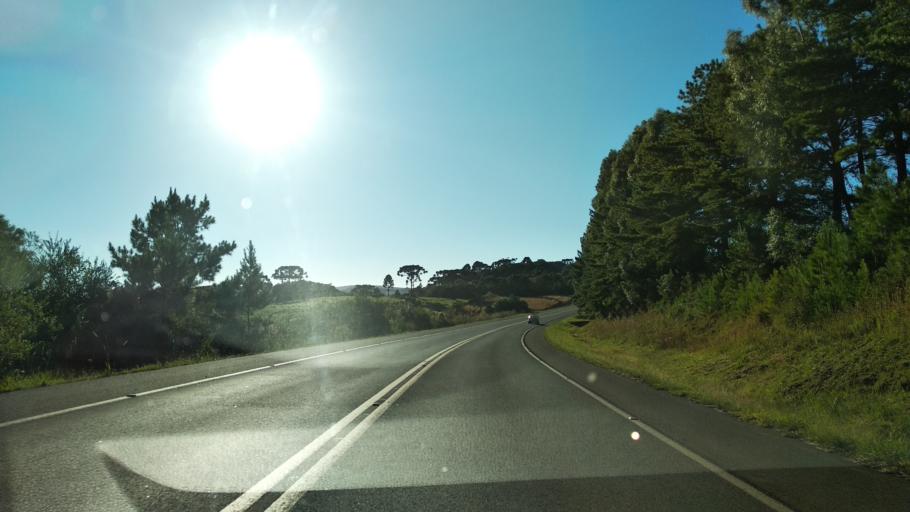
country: BR
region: Santa Catarina
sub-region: Lages
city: Lages
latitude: -27.7849
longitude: -50.4476
